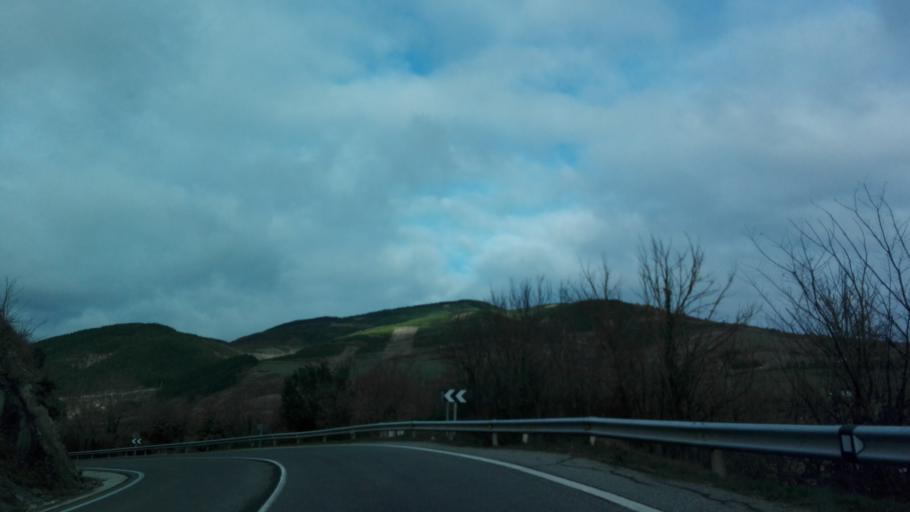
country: ES
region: Navarre
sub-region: Provincia de Navarra
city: Atarrabia
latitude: 42.8357
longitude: -1.6048
